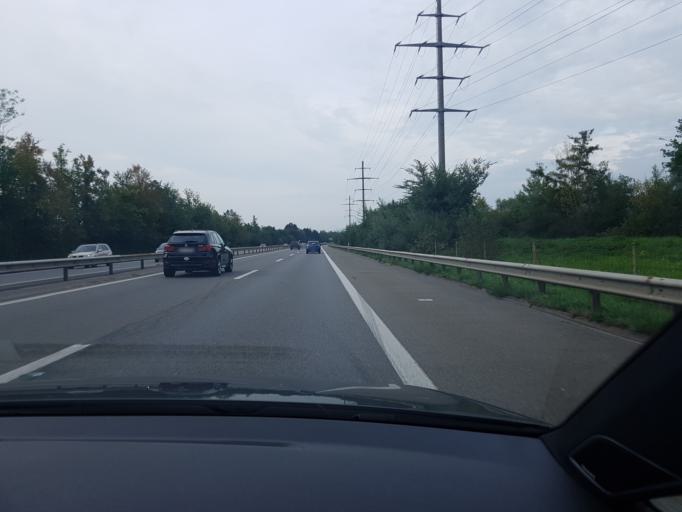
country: CH
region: Lucerne
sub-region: Lucerne-Land District
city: Root
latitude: 47.1304
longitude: 8.3971
